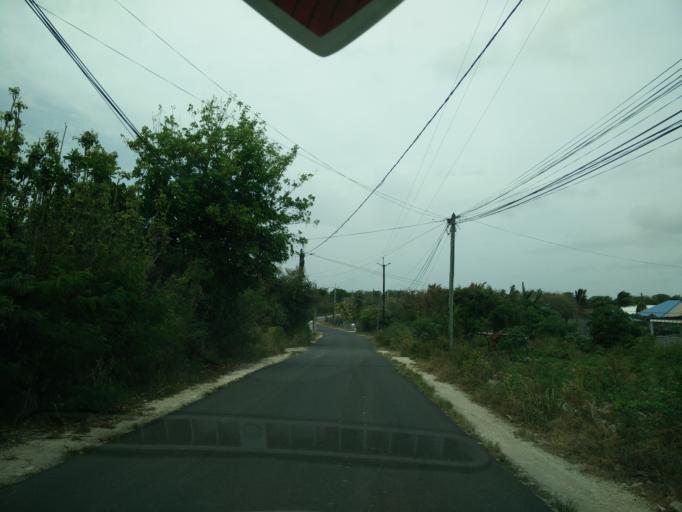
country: GP
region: Guadeloupe
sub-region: Guadeloupe
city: Le Moule
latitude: 16.3214
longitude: -61.3010
